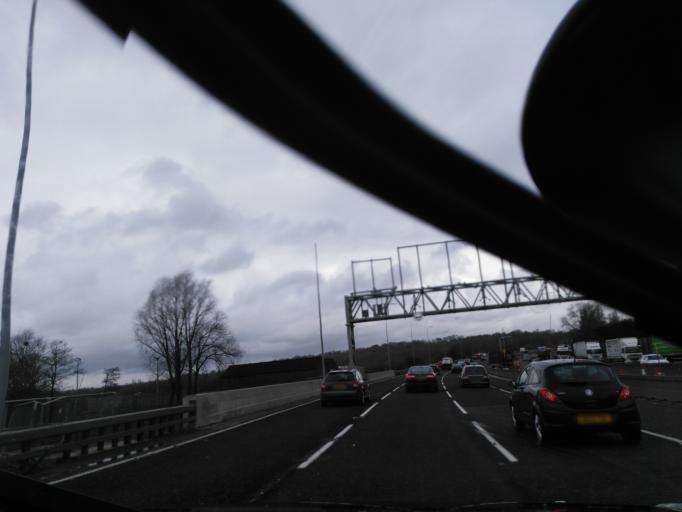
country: GB
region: England
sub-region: City and Borough of Salford
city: Walkden
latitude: 53.4941
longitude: -2.3831
